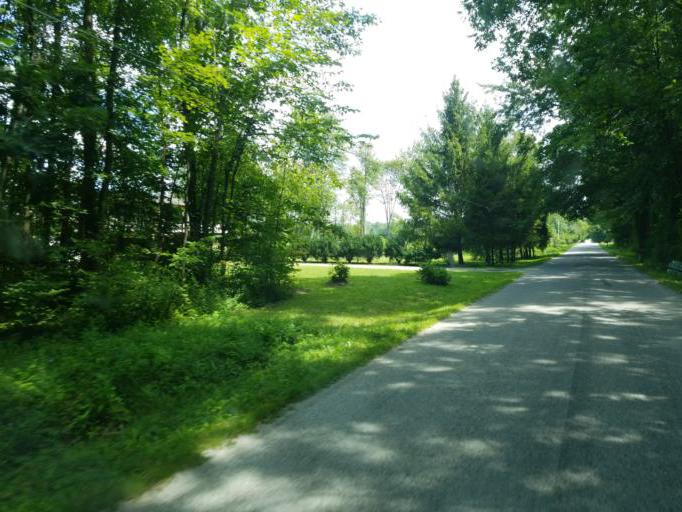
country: US
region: Ohio
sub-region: Delaware County
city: Sunbury
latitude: 40.3378
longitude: -82.8078
